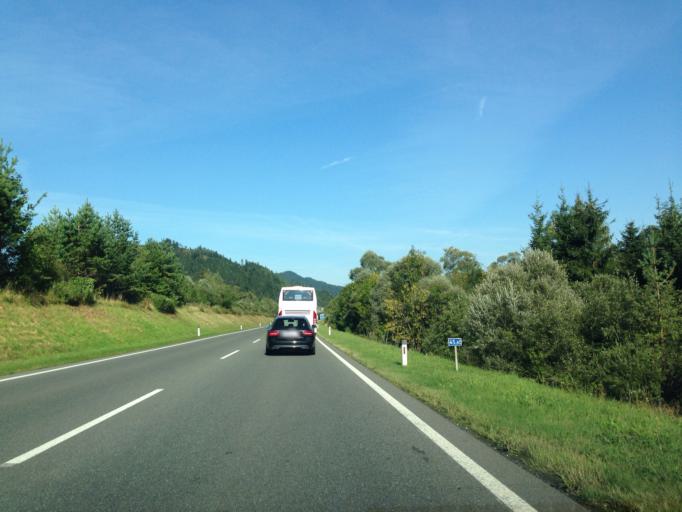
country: AT
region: Tyrol
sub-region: Politischer Bezirk Reutte
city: Musau
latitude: 47.5349
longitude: 10.6766
